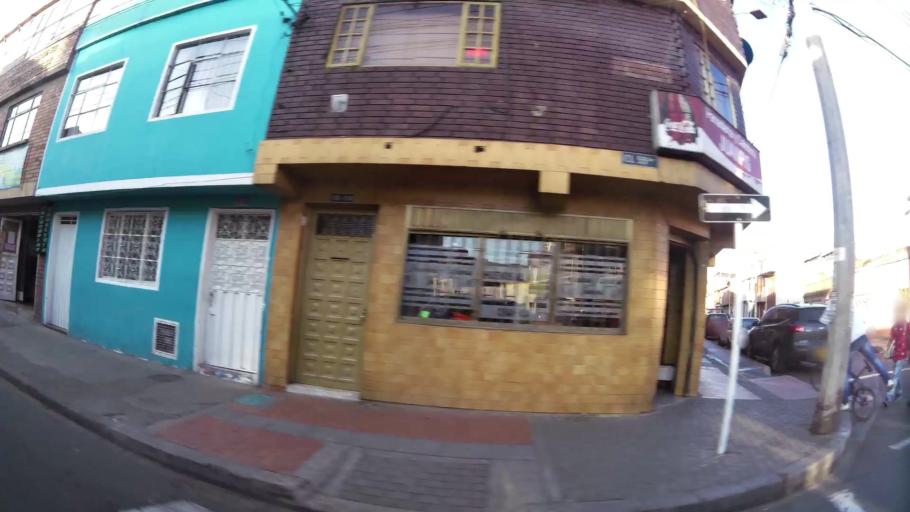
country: CO
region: Bogota D.C.
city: Bogota
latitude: 4.5668
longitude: -74.1322
